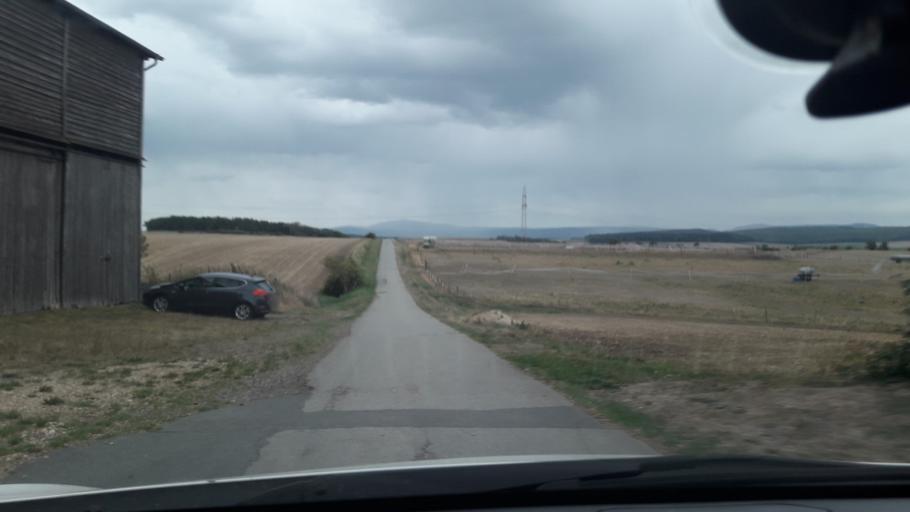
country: DE
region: Lower Saxony
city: Gielde
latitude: 52.0220
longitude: 10.4722
